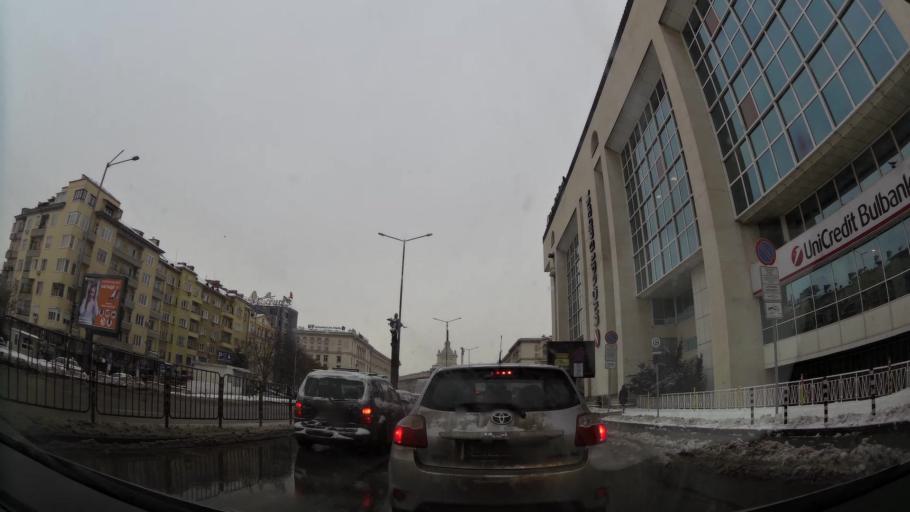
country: BG
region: Sofia-Capital
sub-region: Stolichna Obshtina
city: Sofia
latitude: 42.6980
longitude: 23.3200
